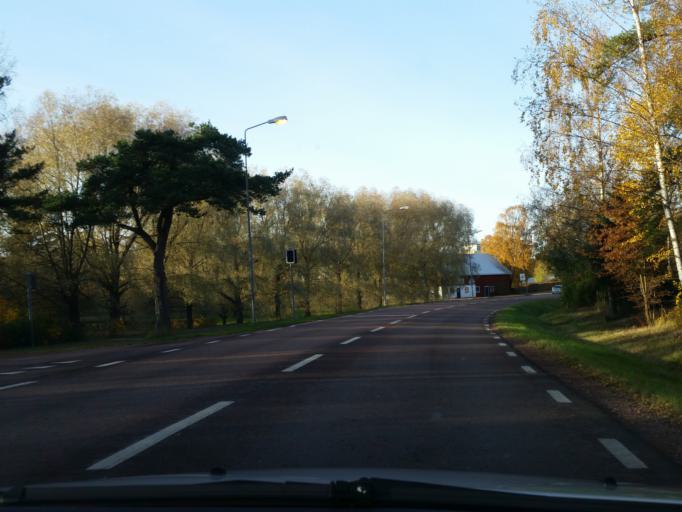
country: AX
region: Mariehamns stad
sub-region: Mariehamn
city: Mariehamn
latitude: 60.1074
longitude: 19.9314
